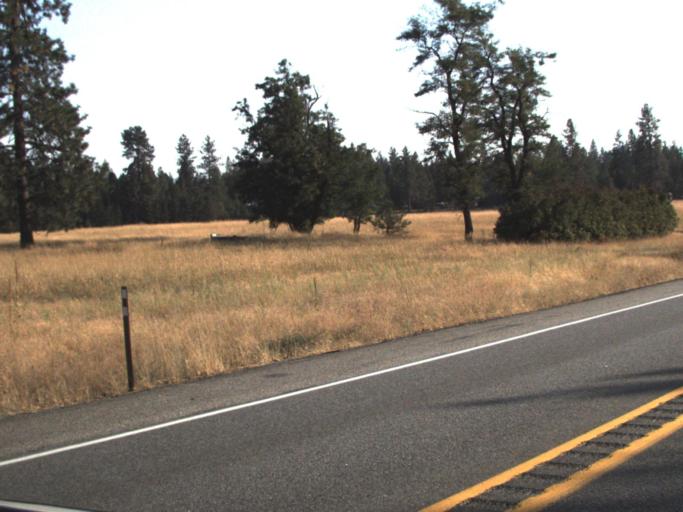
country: US
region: Washington
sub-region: Spokane County
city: Deer Park
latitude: 48.0388
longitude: -117.3490
